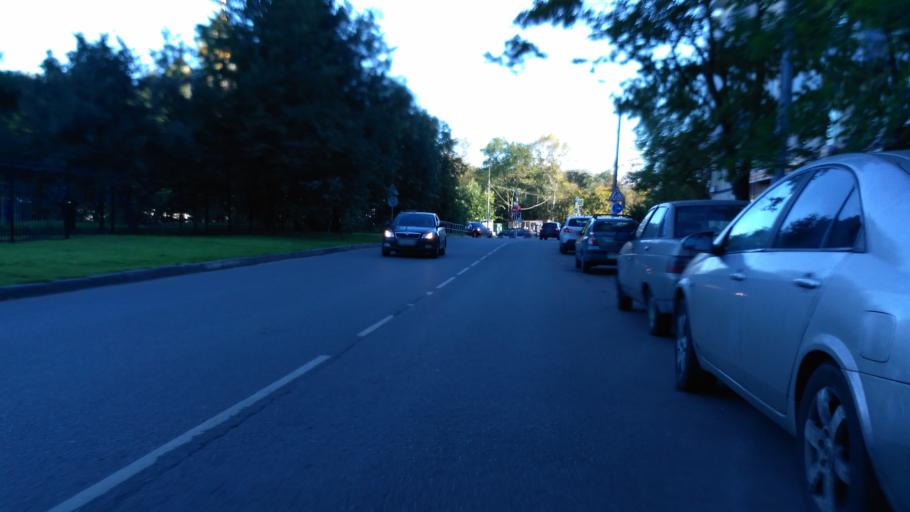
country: RU
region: Moscow
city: Zapadnoye Degunino
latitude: 55.8845
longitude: 37.5328
